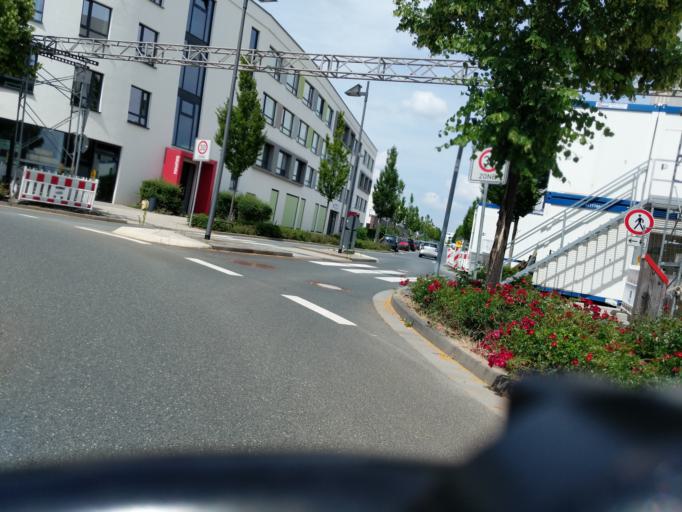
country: DE
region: Hesse
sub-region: Regierungsbezirk Darmstadt
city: Bad Homburg vor der Hoehe
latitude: 50.1751
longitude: 8.6329
